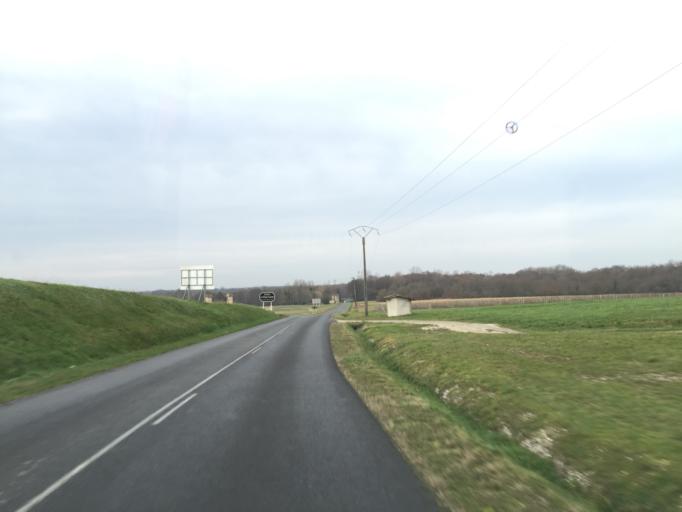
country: FR
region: Aquitaine
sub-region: Departement de la Gironde
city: Pauillac
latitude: 45.1528
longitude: -0.7904
